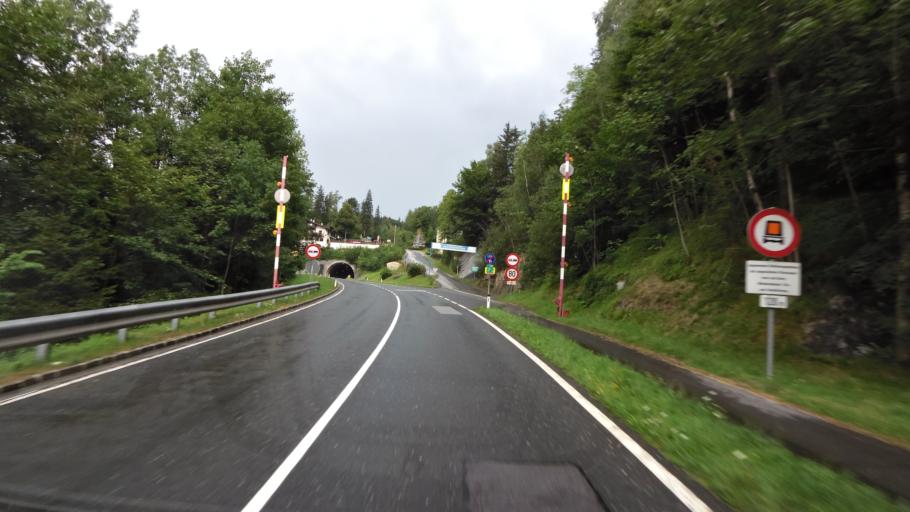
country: AT
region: Salzburg
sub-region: Politischer Bezirk Hallein
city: Scheffau am Tennengebirge
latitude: 47.5740
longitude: 13.1949
